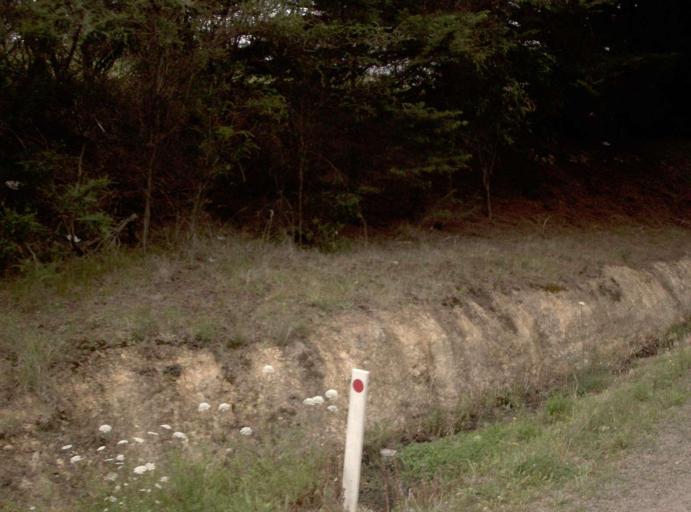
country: AU
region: Victoria
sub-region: Yarra Ranges
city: Lilydale
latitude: -37.7171
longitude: 145.3800
